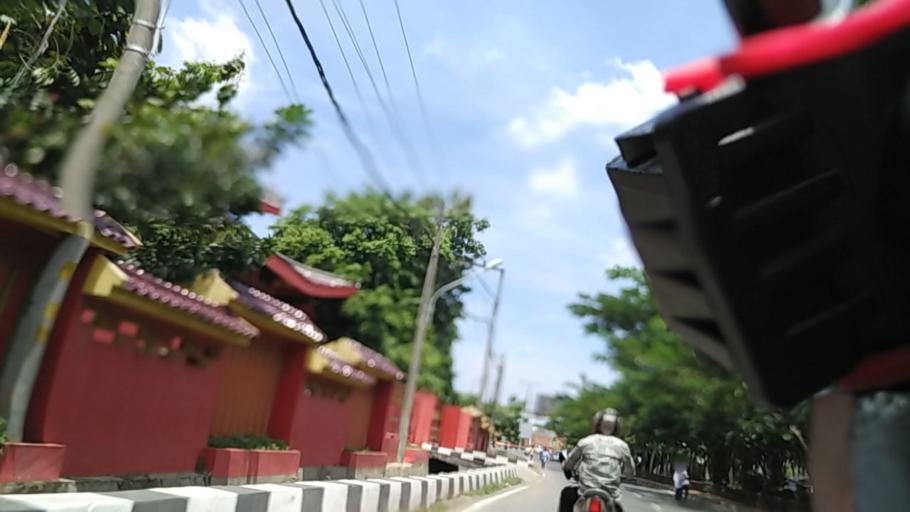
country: ID
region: Central Java
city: Semarang
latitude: -6.9965
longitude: 110.3992
